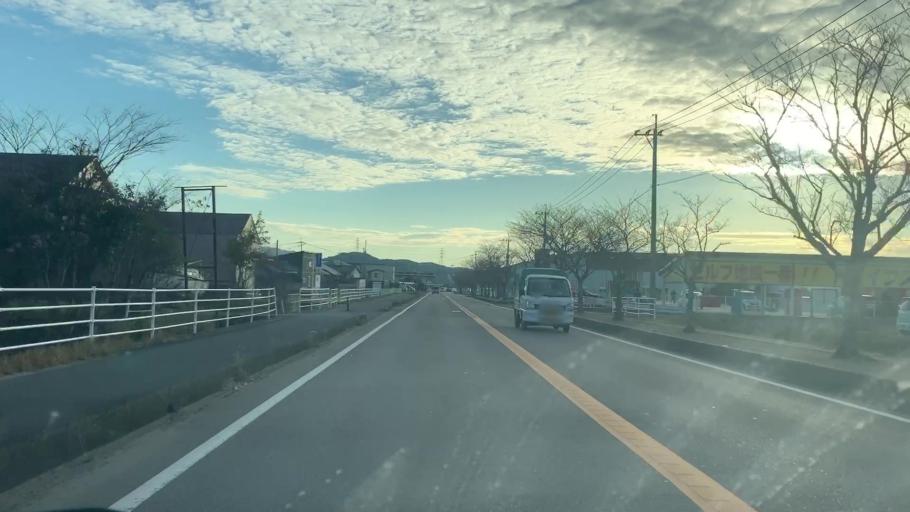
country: JP
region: Saga Prefecture
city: Karatsu
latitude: 33.4126
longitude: 129.9931
